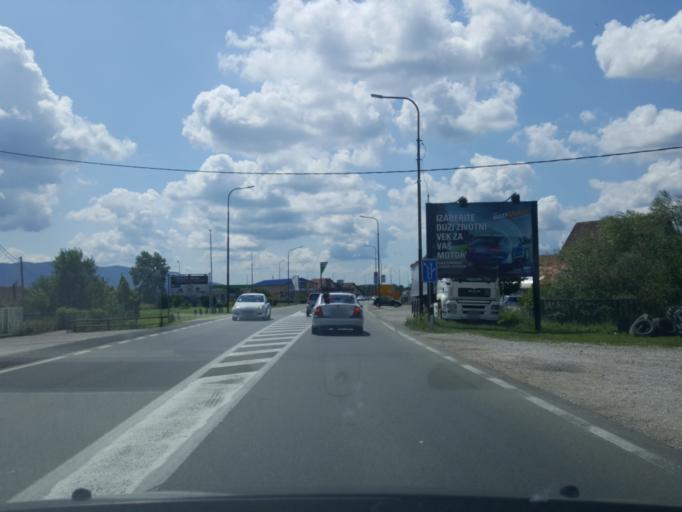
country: RS
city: Lipnicki Sor
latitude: 44.5759
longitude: 19.2435
